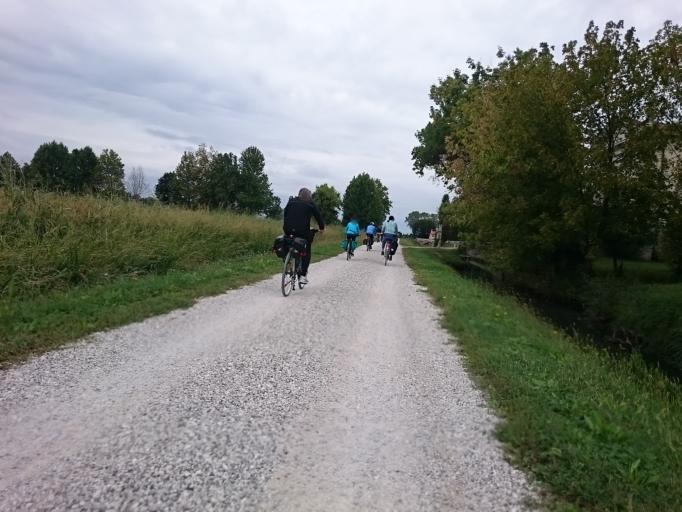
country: IT
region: Veneto
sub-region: Provincia di Vicenza
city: Grumolo delle Abbadesse
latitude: 45.4969
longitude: 11.6643
